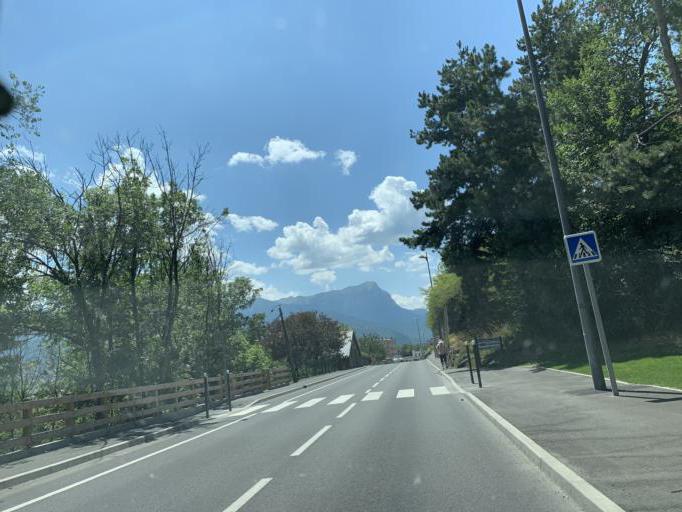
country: FR
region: Provence-Alpes-Cote d'Azur
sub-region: Departement des Hautes-Alpes
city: Embrun
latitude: 44.5614
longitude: 6.4894
